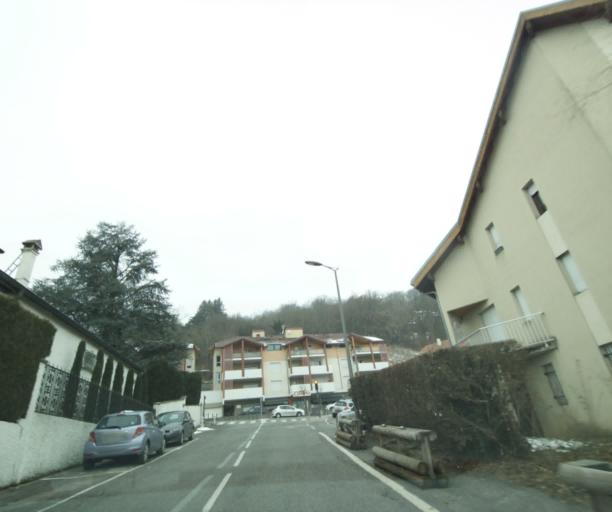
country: FR
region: Rhone-Alpes
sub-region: Departement de la Haute-Savoie
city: Vetraz-Monthoux
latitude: 46.1639
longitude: 6.2373
